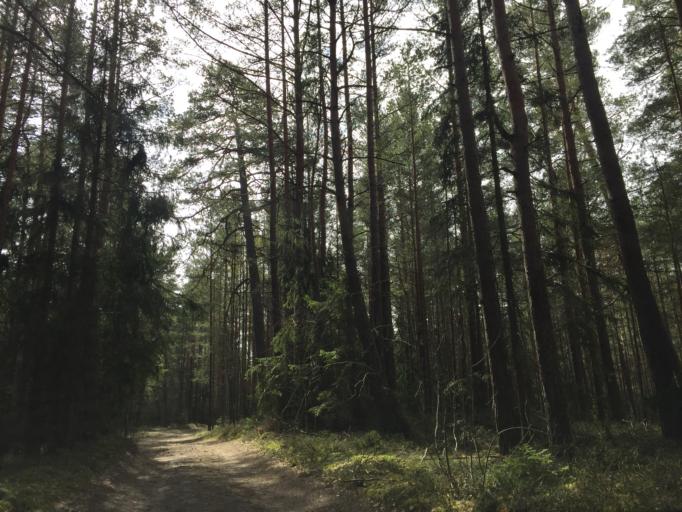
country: LV
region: Salacgrivas
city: Salacgriva
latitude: 57.6925
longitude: 24.3604
